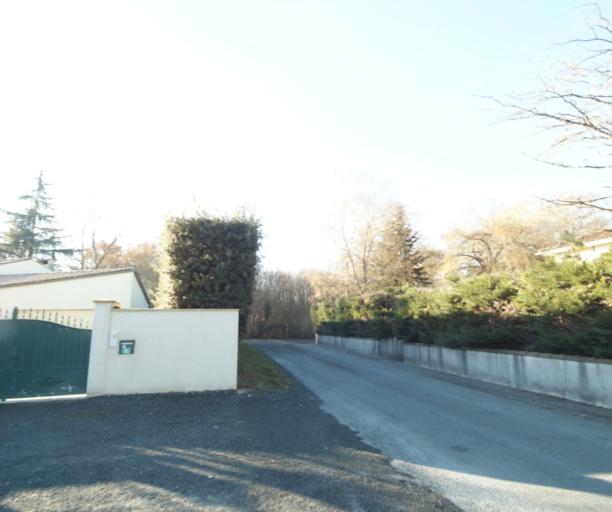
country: FR
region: Poitou-Charentes
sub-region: Departement de la Charente-Maritime
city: Fontcouverte
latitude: 45.7656
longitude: -0.5855
